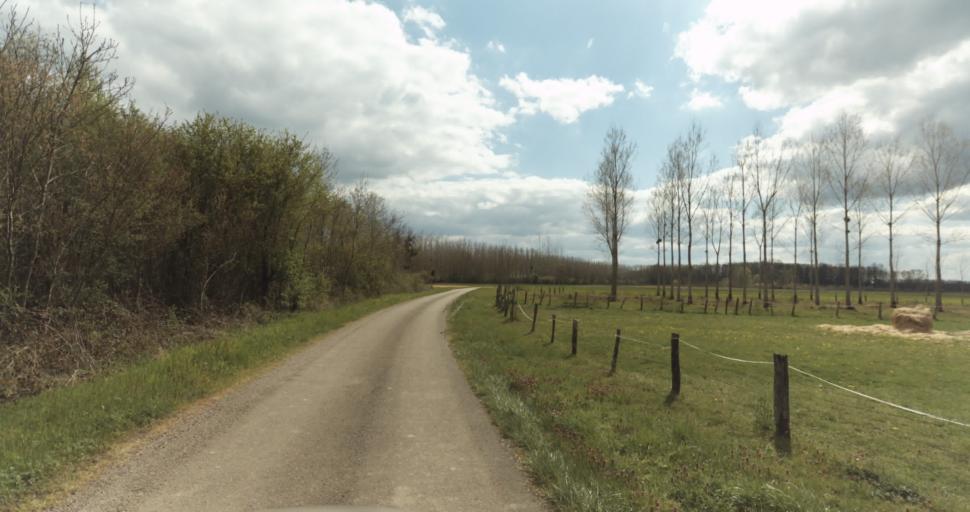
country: FR
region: Bourgogne
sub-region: Departement de la Cote-d'Or
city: Auxonne
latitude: 47.1645
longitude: 5.3959
